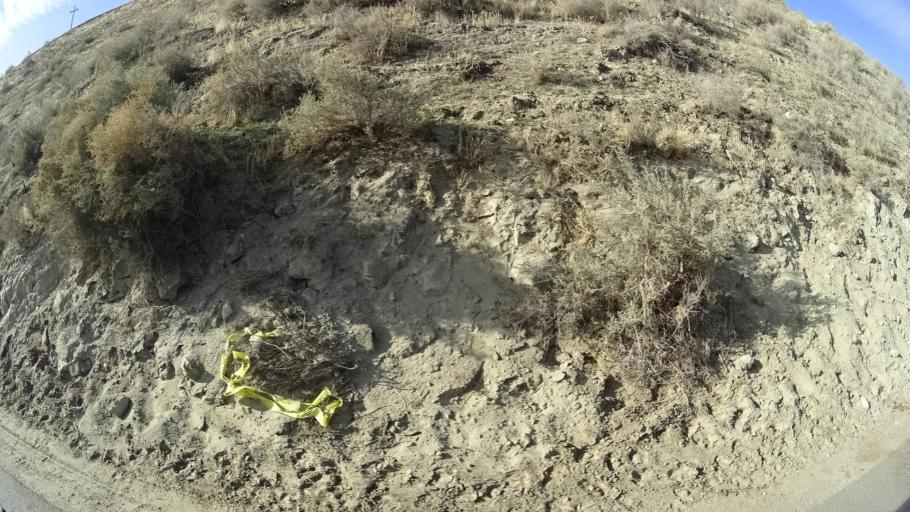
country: US
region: California
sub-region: Kern County
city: Oildale
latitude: 35.5142
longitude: -118.9006
